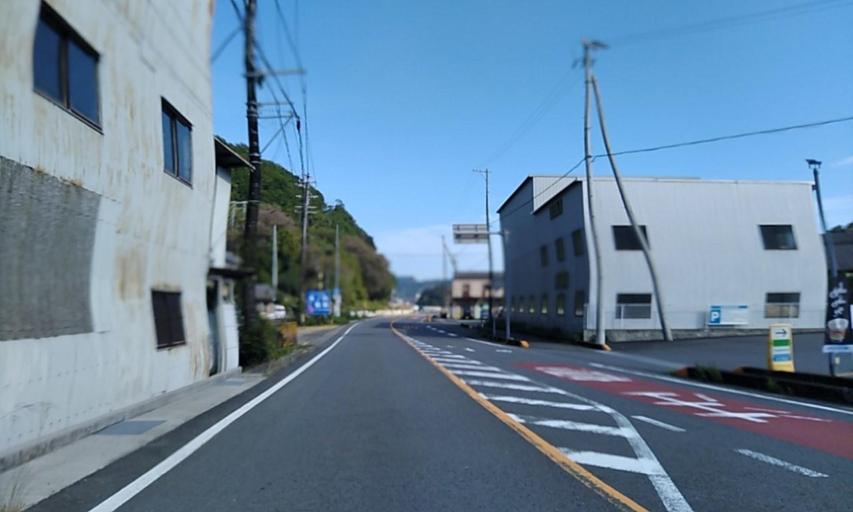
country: JP
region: Mie
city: Owase
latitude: 34.1963
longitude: 136.3205
